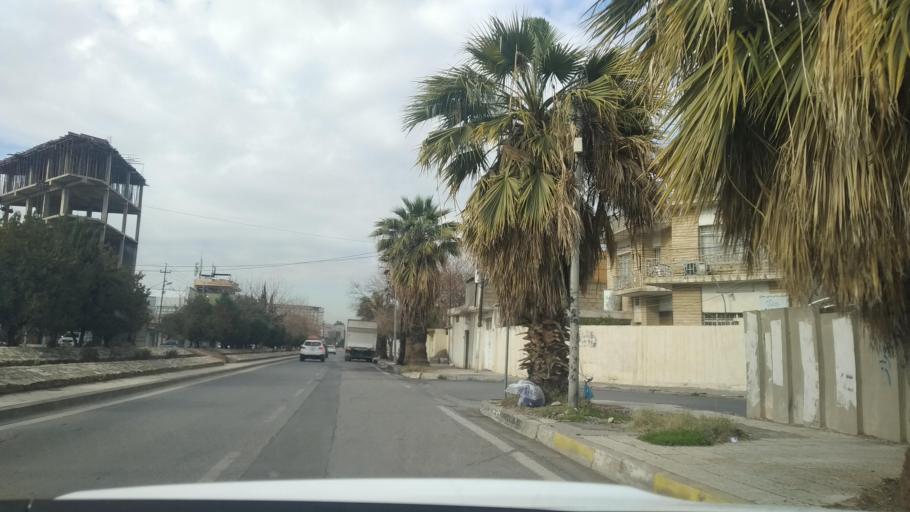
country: IQ
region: Arbil
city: Erbil
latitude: 36.1800
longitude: 44.0211
